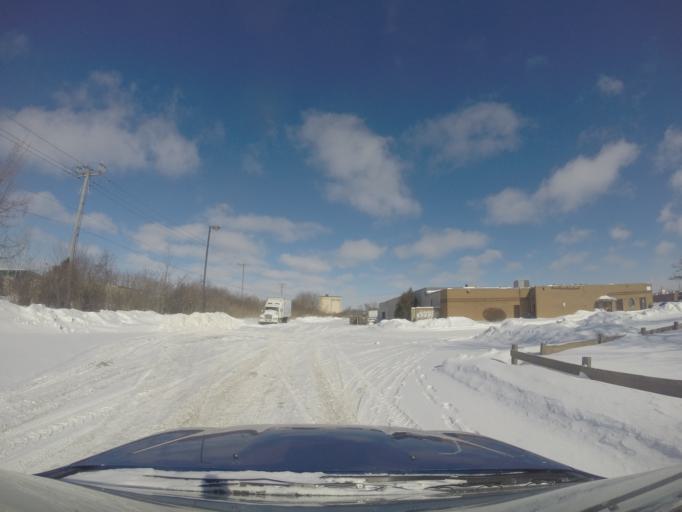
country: CA
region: Ontario
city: Cambridge
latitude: 43.4010
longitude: -80.3285
